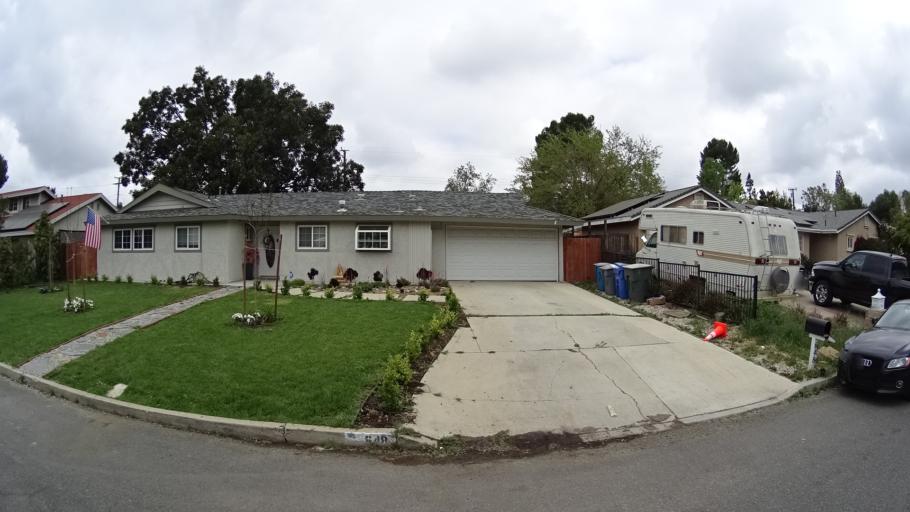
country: US
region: California
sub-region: Ventura County
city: Thousand Oaks
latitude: 34.2144
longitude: -118.8642
